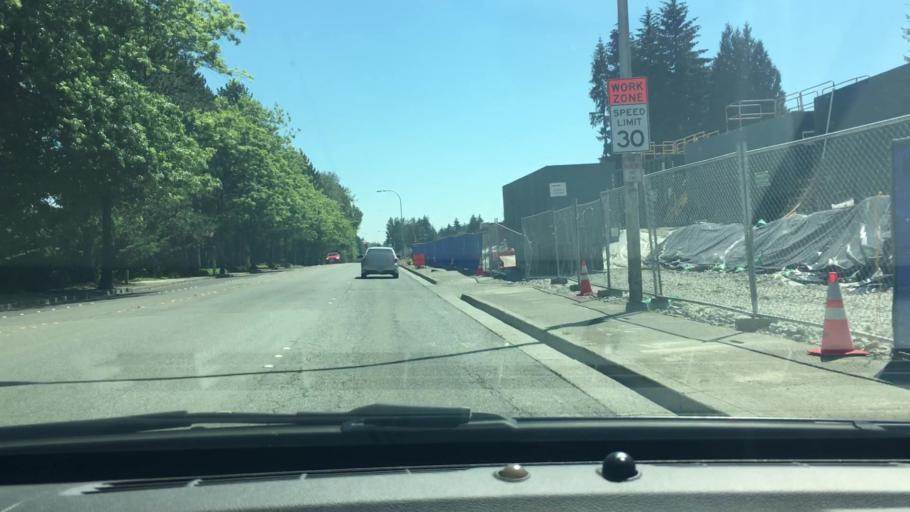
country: US
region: Washington
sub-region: King County
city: Bellevue
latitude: 47.6067
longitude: -122.1909
